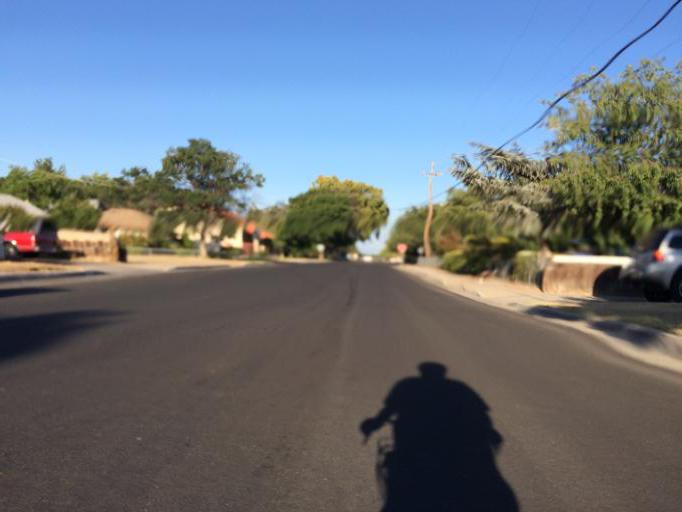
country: US
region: California
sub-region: Fresno County
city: Clovis
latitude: 36.8208
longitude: -119.7064
